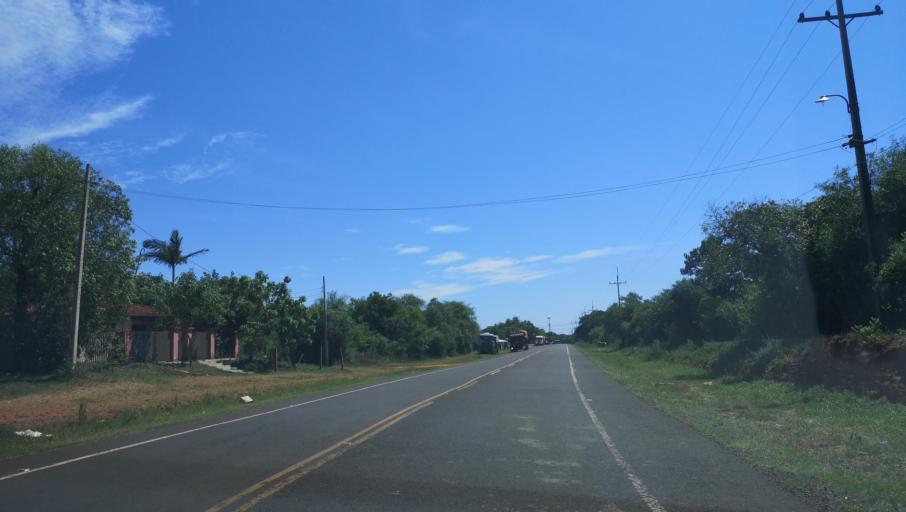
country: PY
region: Misiones
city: Santa Maria
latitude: -26.9045
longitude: -57.0285
